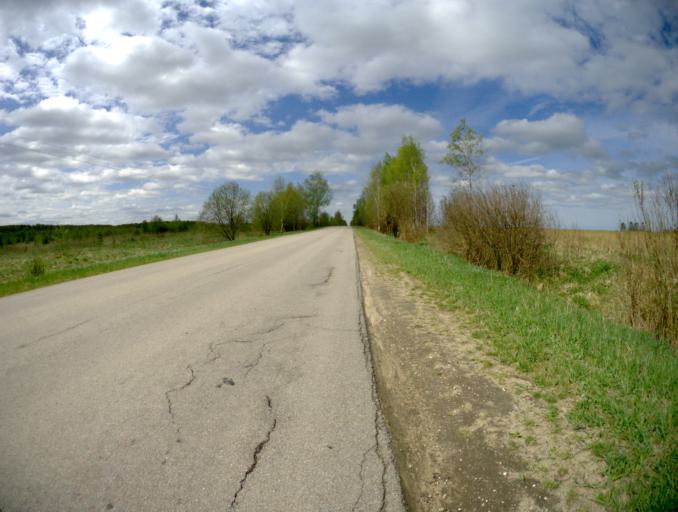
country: RU
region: Vladimir
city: Golovino
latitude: 55.9585
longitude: 40.4752
